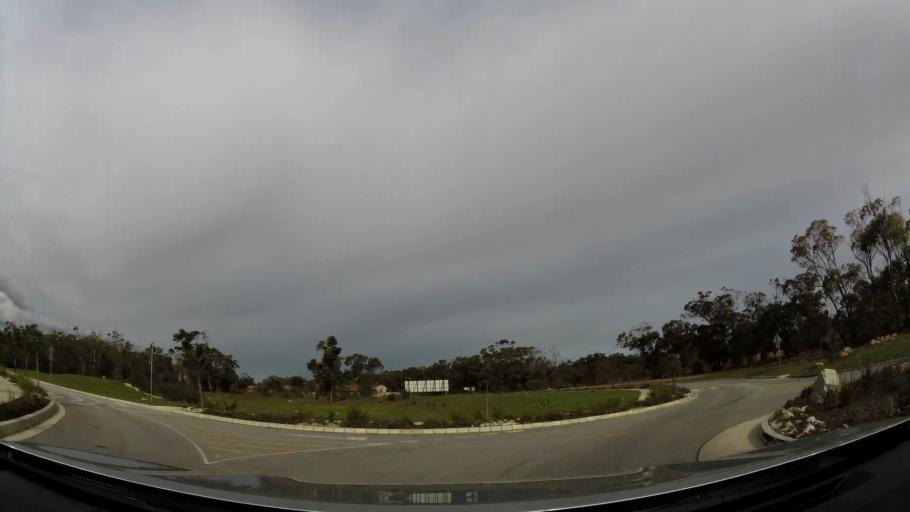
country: ZA
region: Eastern Cape
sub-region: Nelson Mandela Bay Metropolitan Municipality
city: Port Elizabeth
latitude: -33.9334
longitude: 25.4901
